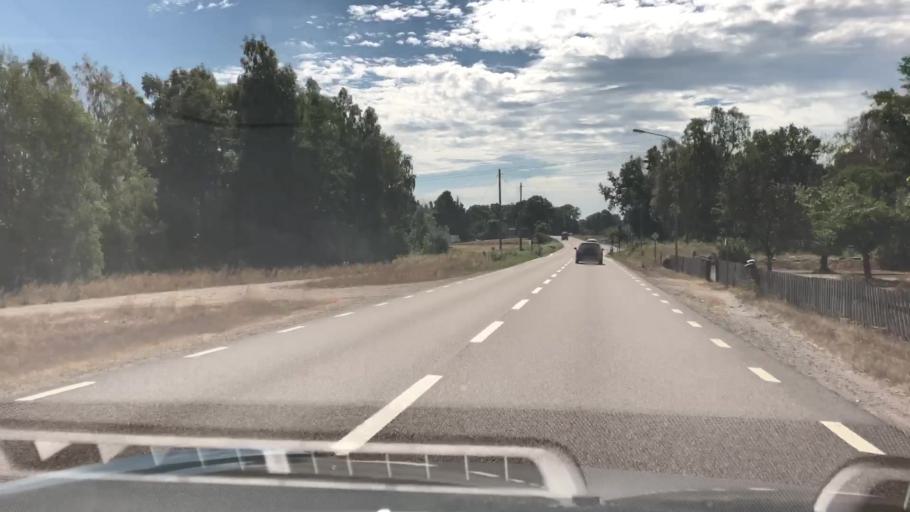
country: SE
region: Kalmar
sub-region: Torsas Kommun
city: Torsas
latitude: 56.3876
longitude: 16.0673
